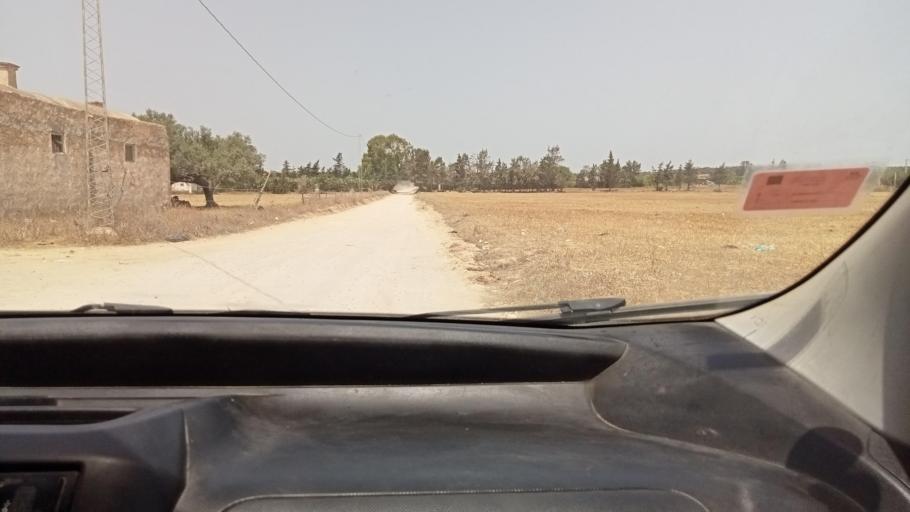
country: TN
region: Nabul
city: Qulaybiyah
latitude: 36.8635
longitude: 11.0842
